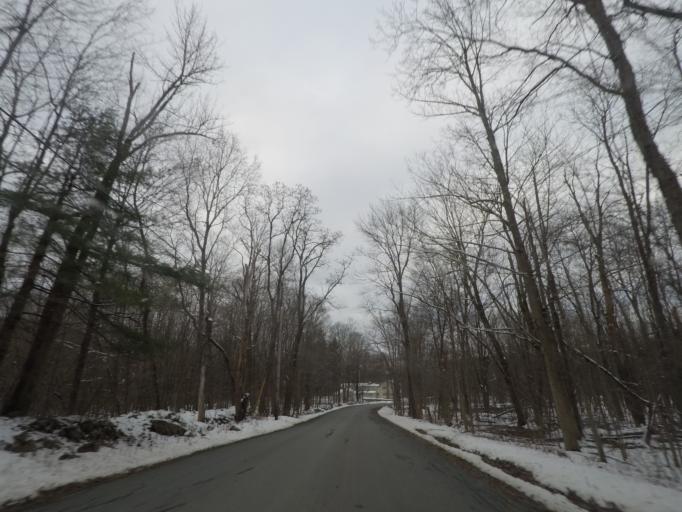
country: US
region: New York
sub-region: Rensselaer County
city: Averill Park
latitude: 42.6458
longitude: -73.5376
